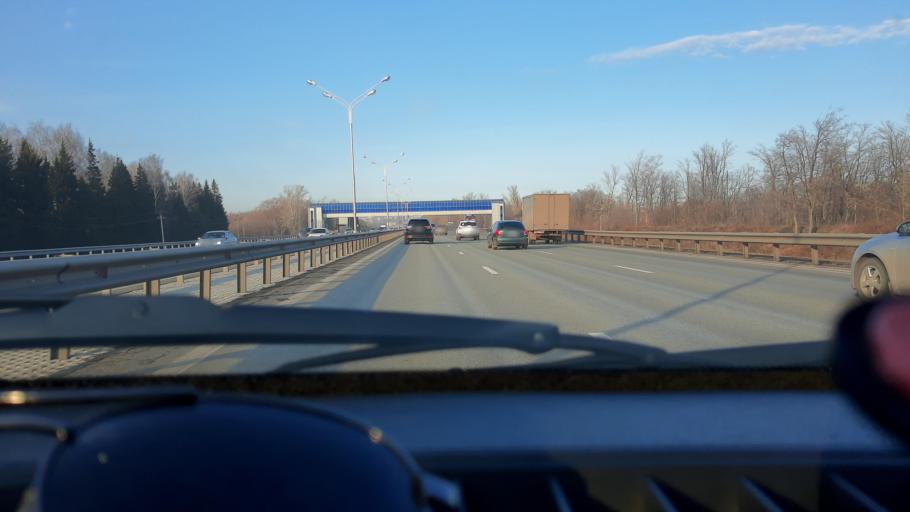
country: RU
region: Bashkortostan
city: Ufa
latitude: 54.6534
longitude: 55.9332
